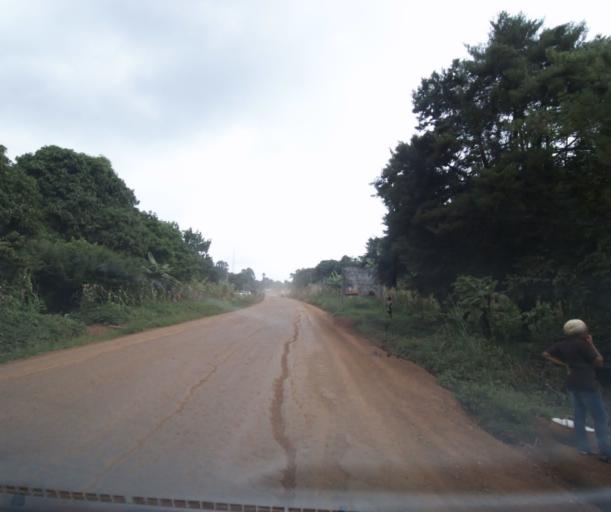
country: CM
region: West
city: Mbouda
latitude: 5.6738
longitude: 10.2129
